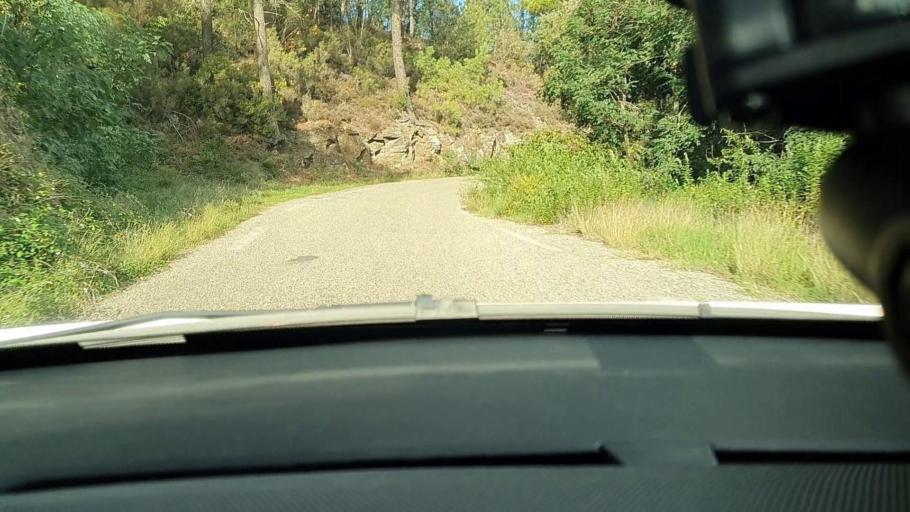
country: FR
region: Languedoc-Roussillon
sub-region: Departement du Gard
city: Besseges
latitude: 44.3255
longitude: 4.0372
